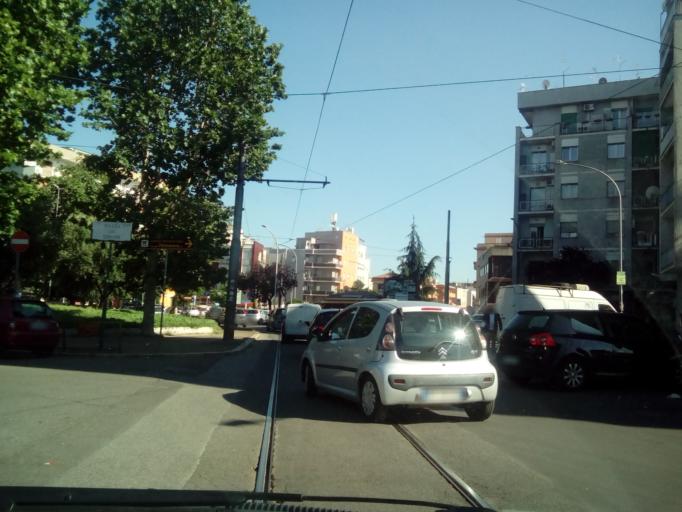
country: IT
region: Latium
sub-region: Citta metropolitana di Roma Capitale
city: Rome
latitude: 41.8858
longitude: 12.5663
